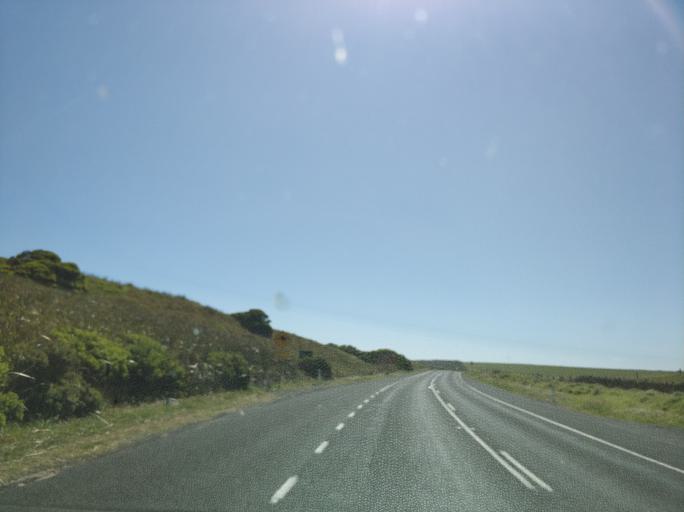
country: AU
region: Victoria
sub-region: Colac-Otway
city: Apollo Bay
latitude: -38.6703
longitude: 143.1156
